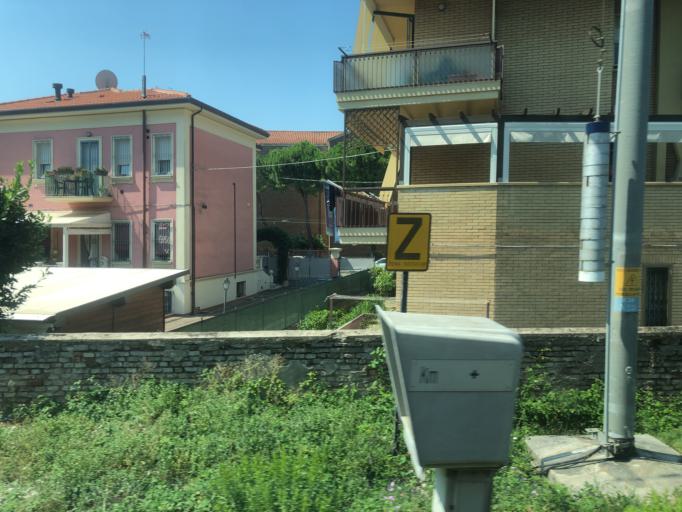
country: IT
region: Emilia-Romagna
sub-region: Provincia di Rimini
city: Rimini
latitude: 44.0659
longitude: 12.5703
